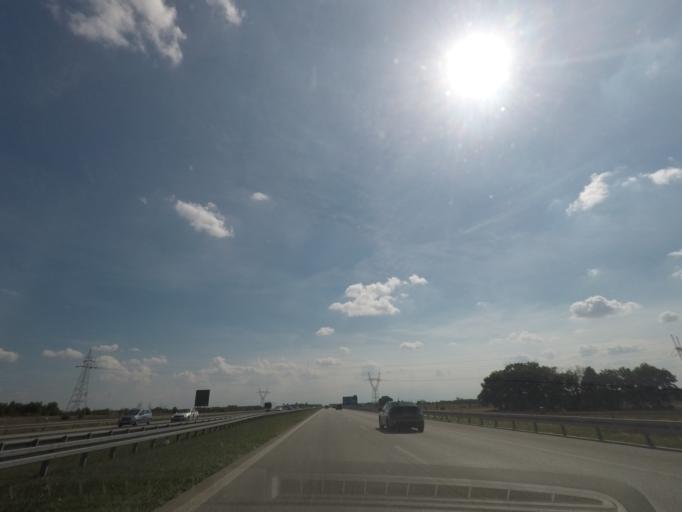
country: PL
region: Lodz Voivodeship
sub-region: Powiat lodzki wschodni
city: Andrespol
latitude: 51.6942
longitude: 19.5995
